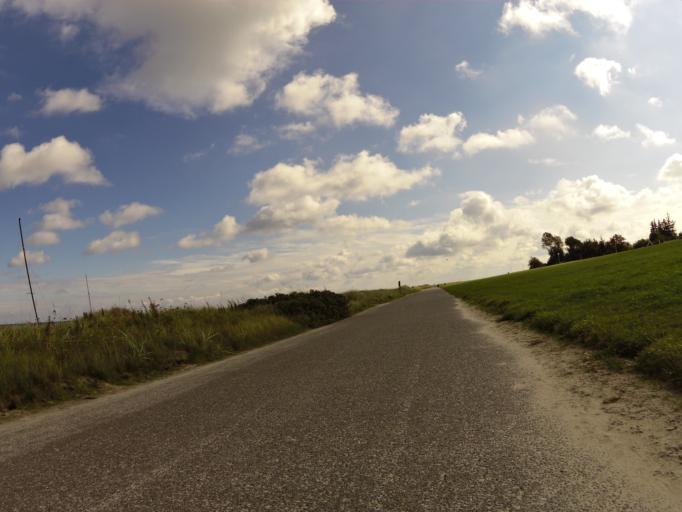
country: DE
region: Schleswig-Holstein
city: Wisch
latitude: 54.4266
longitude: 10.3835
